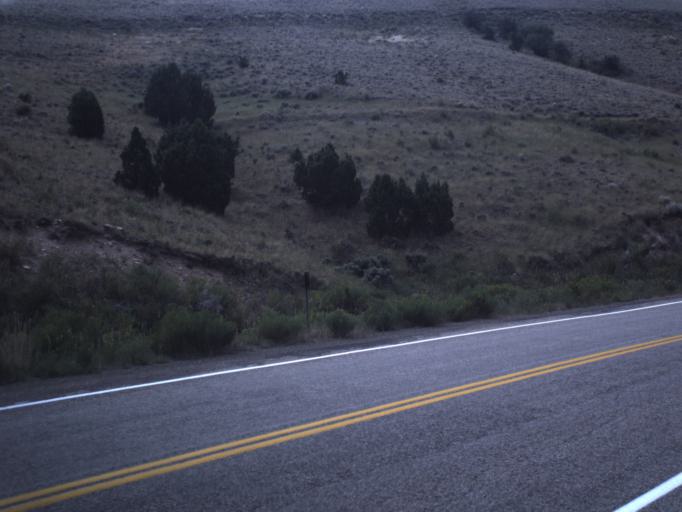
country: US
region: Utah
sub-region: Daggett County
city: Manila
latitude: 40.9108
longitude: -109.6888
